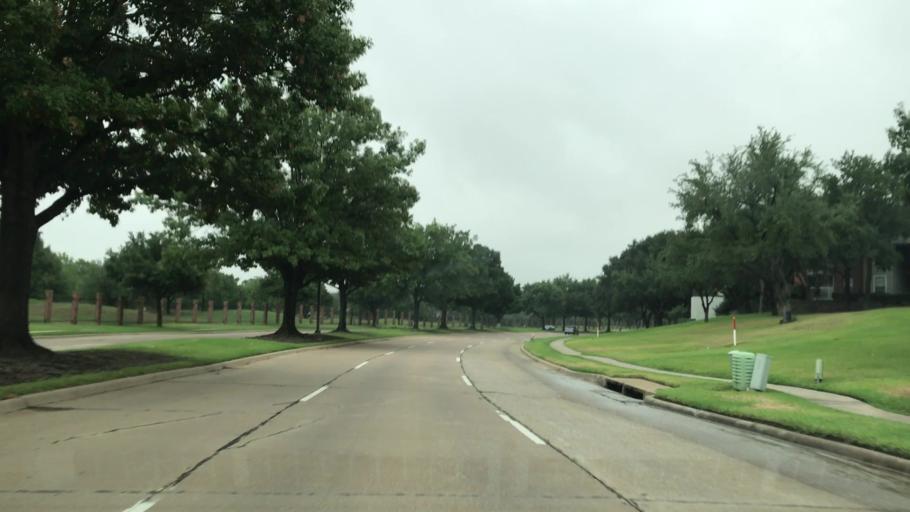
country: US
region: Texas
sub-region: Dallas County
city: Coppell
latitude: 32.9094
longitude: -96.9823
